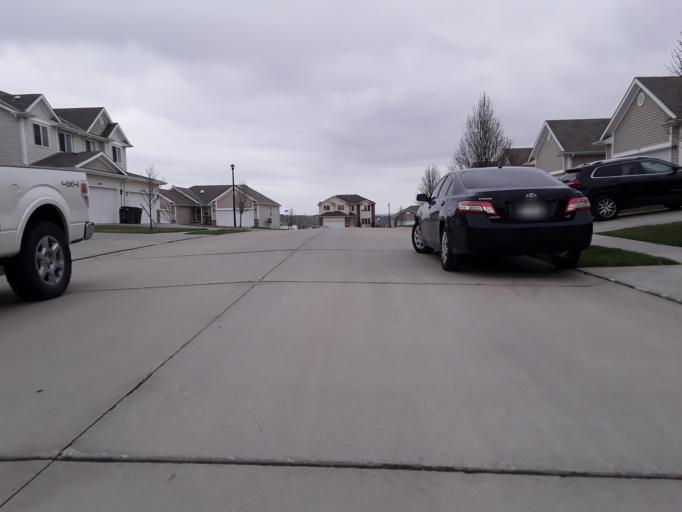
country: US
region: Nebraska
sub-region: Lancaster County
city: Lincoln
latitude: 40.8443
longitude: -96.5995
